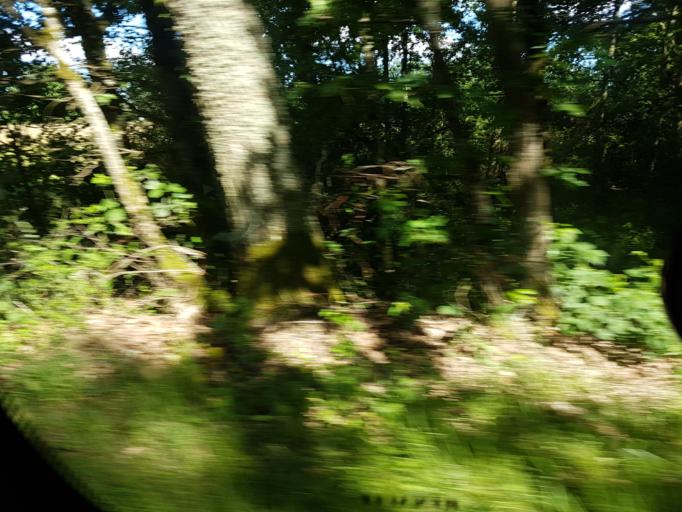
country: FR
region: Bourgogne
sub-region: Departement de Saone-et-Loire
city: Epinac
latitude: 46.9904
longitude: 4.4992
